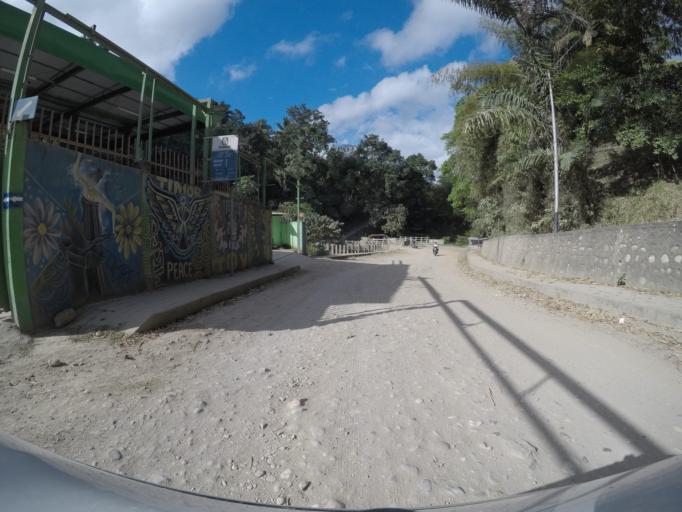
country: TL
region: Viqueque
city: Viqueque
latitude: -8.8661
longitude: 126.3622
